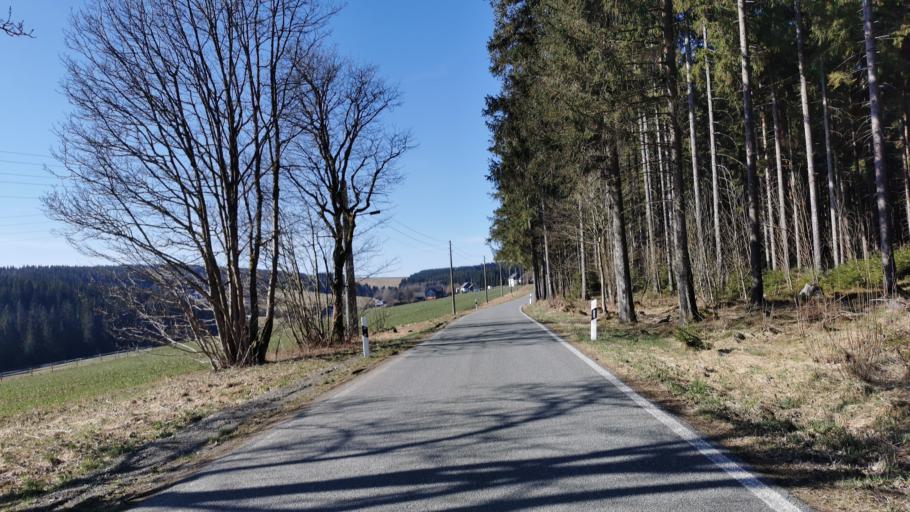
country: DE
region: Thuringia
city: Wurzbach
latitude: 50.4512
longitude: 11.5197
